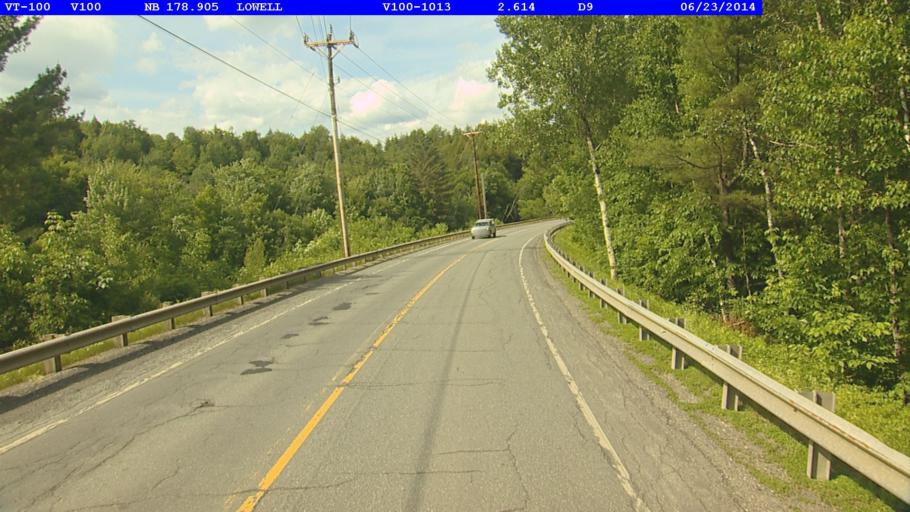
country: US
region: Vermont
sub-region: Lamoille County
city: Hyde Park
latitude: 44.7757
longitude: -72.4567
